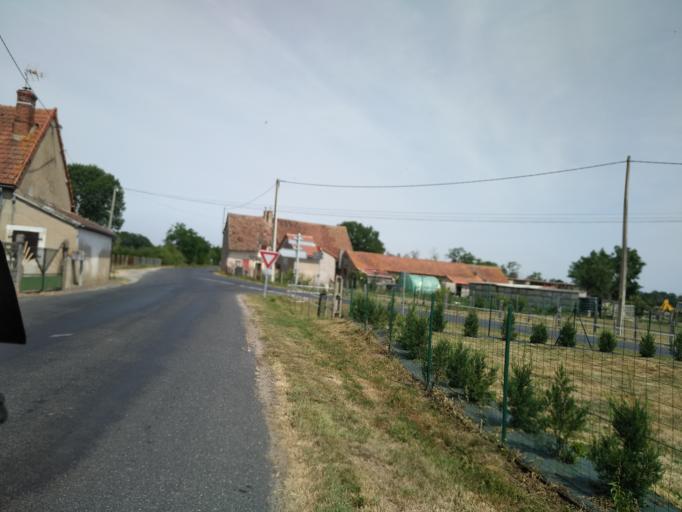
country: FR
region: Bourgogne
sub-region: Departement de Saone-et-Loire
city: Digoin
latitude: 46.4469
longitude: 3.9718
